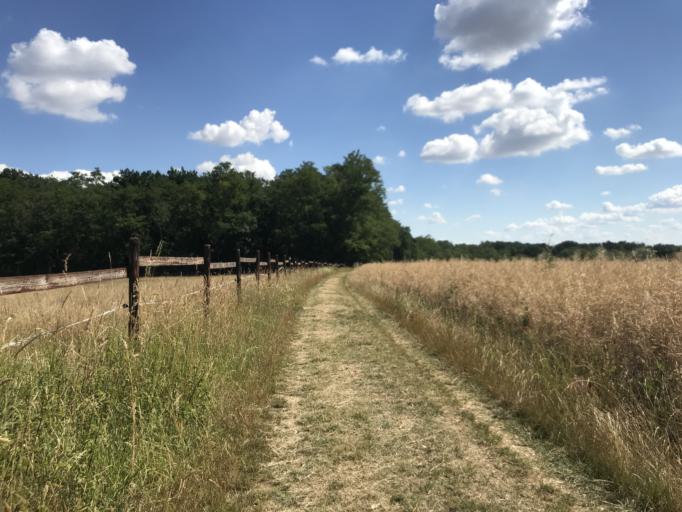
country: DE
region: Rheinland-Pfalz
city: Bubenheim
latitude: 49.9317
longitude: 8.0600
